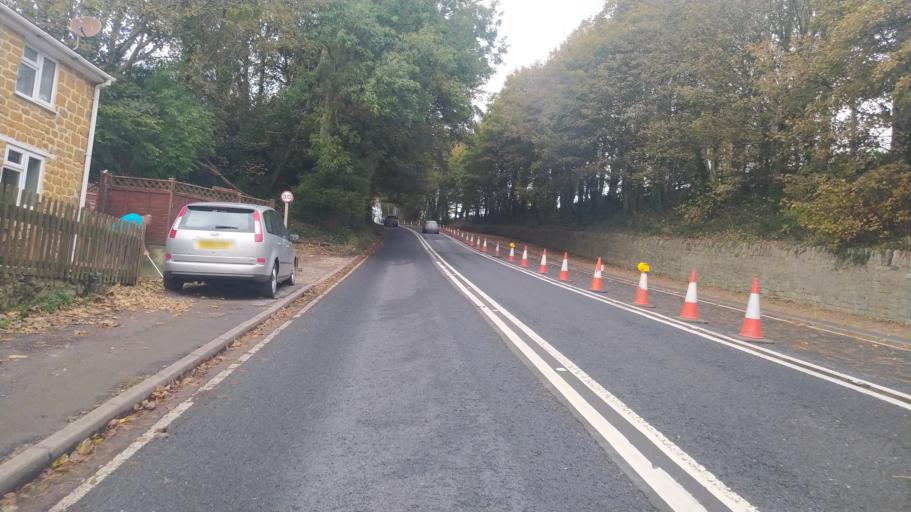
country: GB
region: England
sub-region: Dorset
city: Bridport
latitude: 50.7348
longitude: -2.8282
